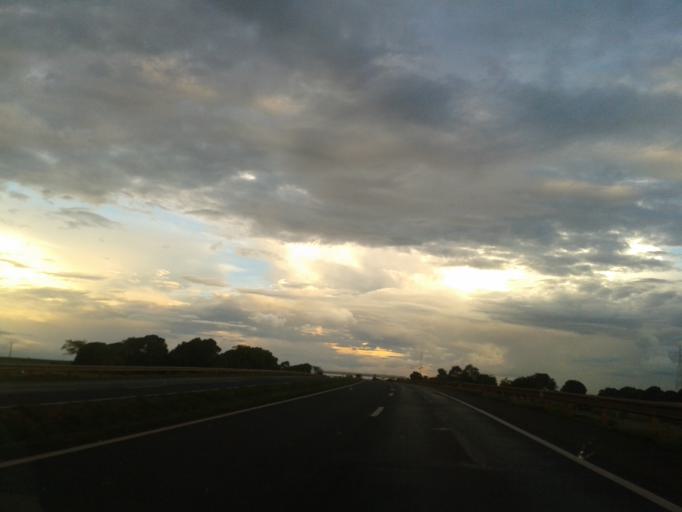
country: BR
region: Minas Gerais
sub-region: Centralina
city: Centralina
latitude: -18.7103
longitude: -49.1378
